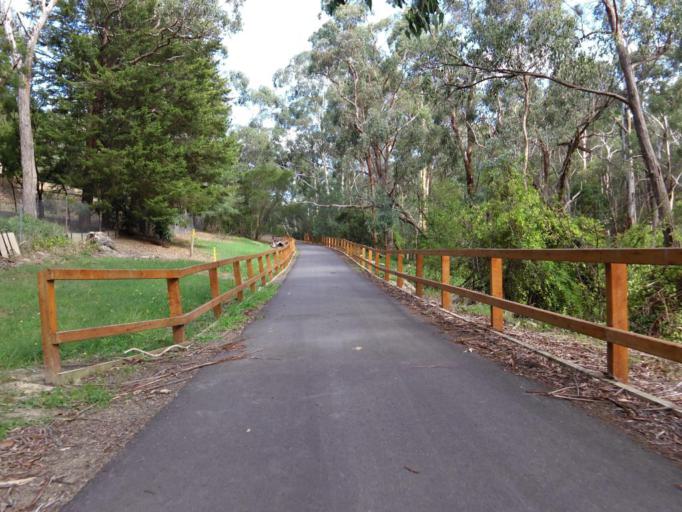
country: AU
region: Victoria
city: Mitcham
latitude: -37.8011
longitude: 145.2030
